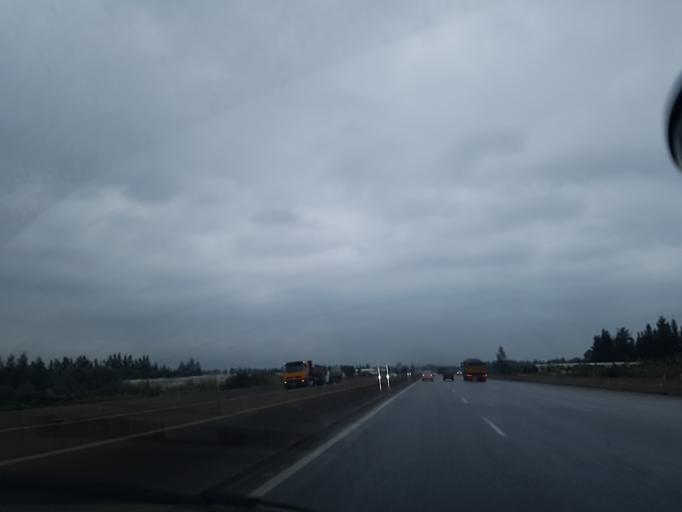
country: DZ
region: Boumerdes
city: Khemis el Khechna
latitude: 36.6681
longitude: 3.2869
